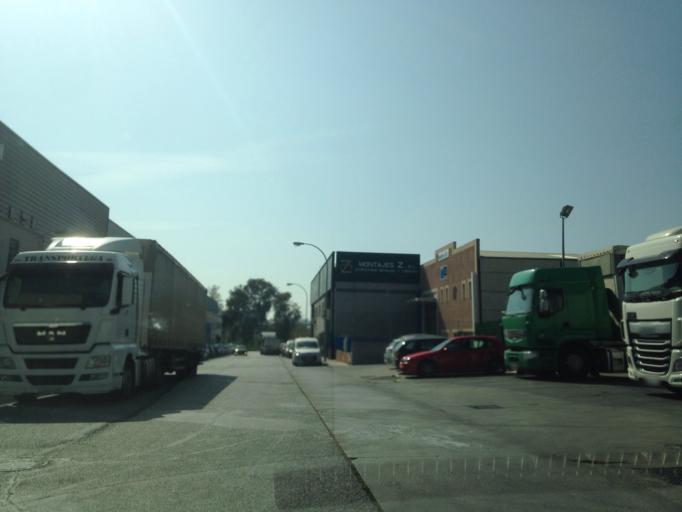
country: ES
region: Andalusia
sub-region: Provincia de Malaga
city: Malaga
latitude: 36.7098
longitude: -4.4702
